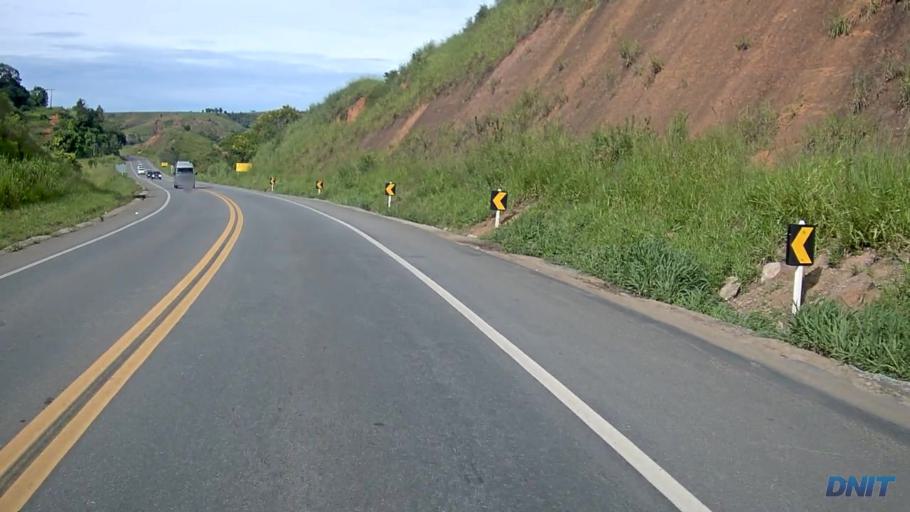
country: BR
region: Minas Gerais
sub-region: Belo Oriente
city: Belo Oriente
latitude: -19.2644
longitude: -42.3466
